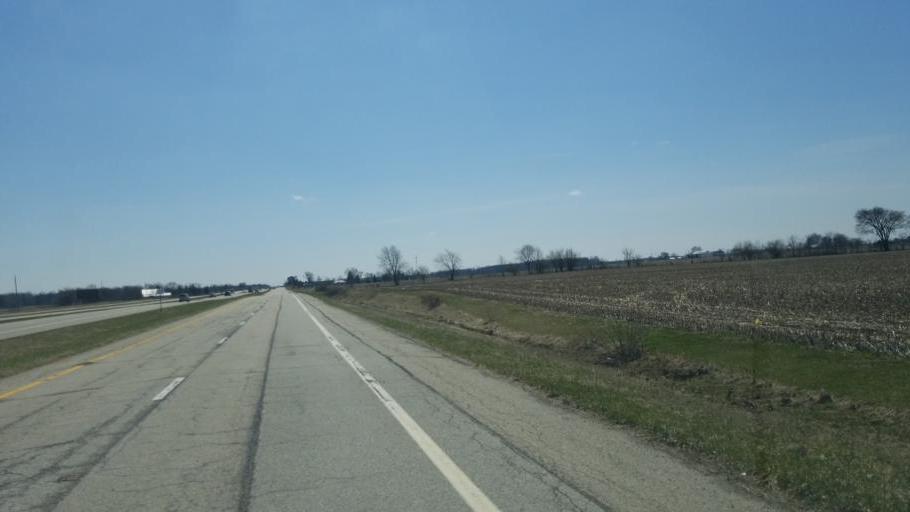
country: US
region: Ohio
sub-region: Delaware County
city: Delaware
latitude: 40.4024
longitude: -83.0746
